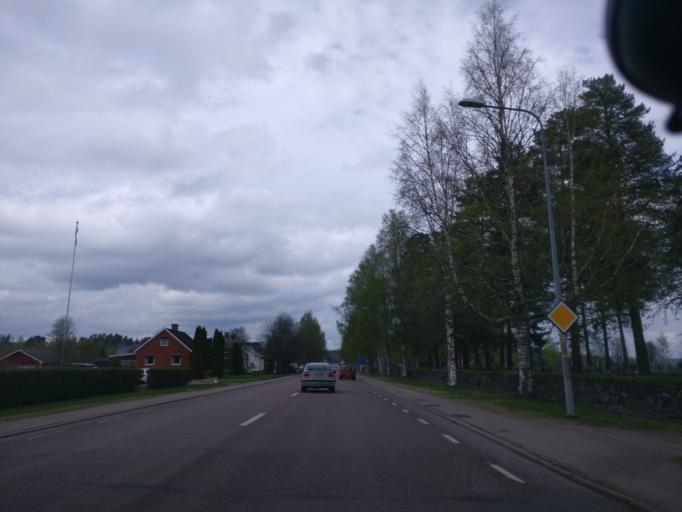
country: SE
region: Vaermland
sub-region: Hagfors Kommun
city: Ekshaerad
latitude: 60.1696
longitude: 13.4975
